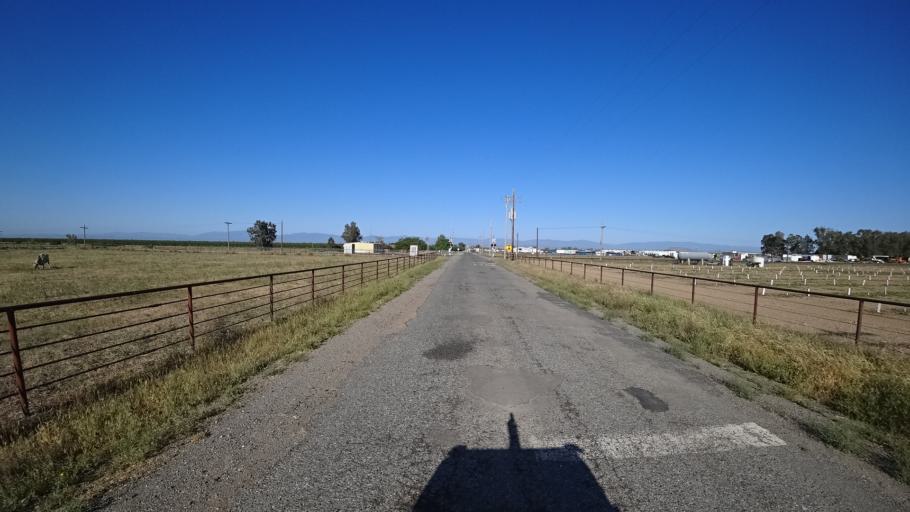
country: US
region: California
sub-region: Glenn County
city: Orland
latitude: 39.6822
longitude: -122.1935
